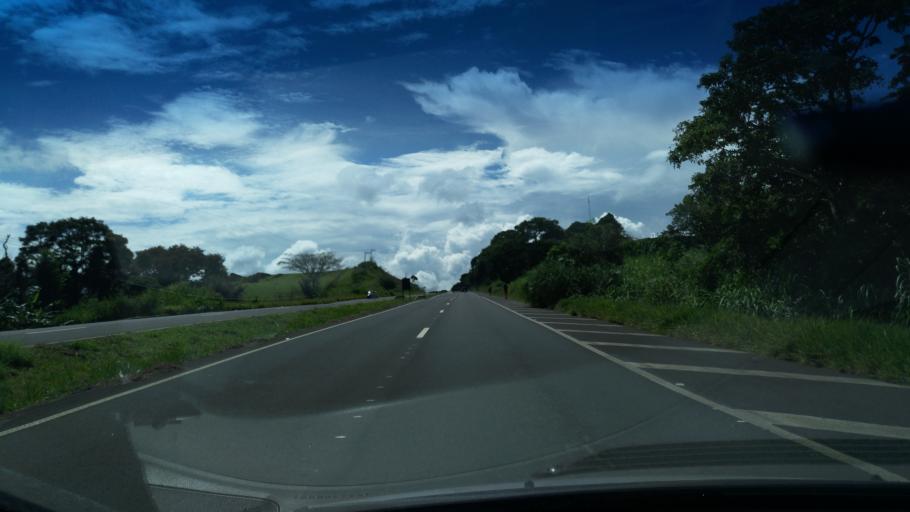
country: BR
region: Sao Paulo
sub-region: Santo Antonio Do Jardim
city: Espirito Santo do Pinhal
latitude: -22.1809
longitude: -46.7569
